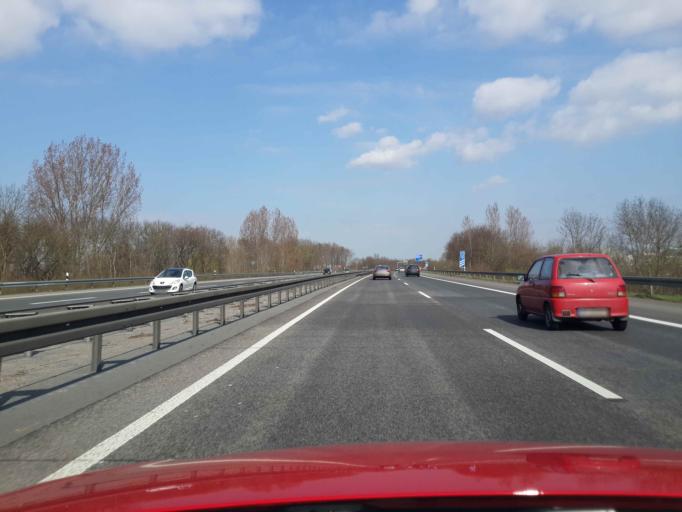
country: DE
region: Hesse
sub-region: Regierungsbezirk Darmstadt
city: Bensheim
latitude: 49.6687
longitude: 8.6018
